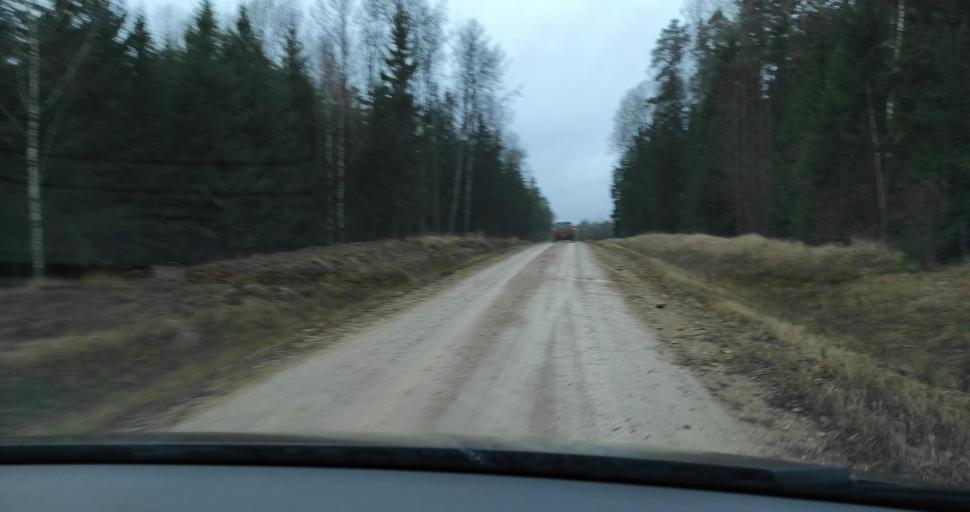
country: LV
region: Skrunda
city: Skrunda
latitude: 56.5549
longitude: 22.0821
